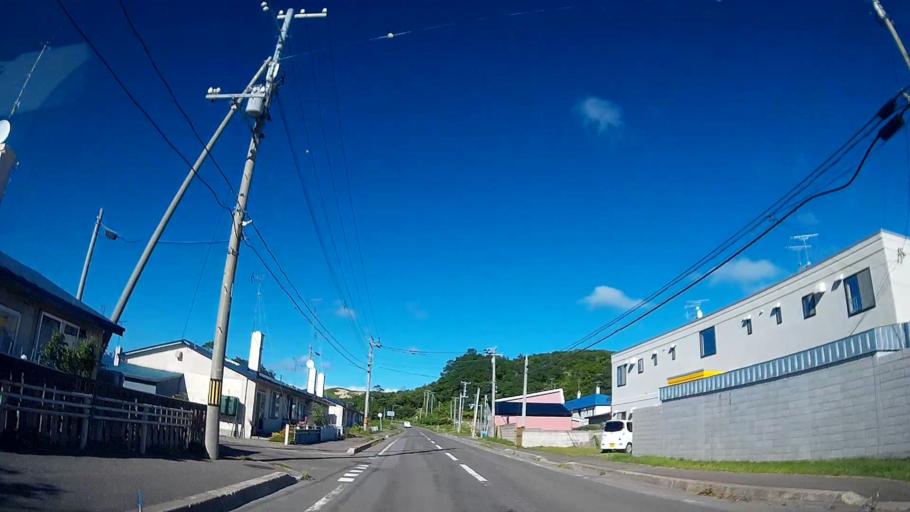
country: JP
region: Hokkaido
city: Iwanai
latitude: 42.4557
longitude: 139.8581
